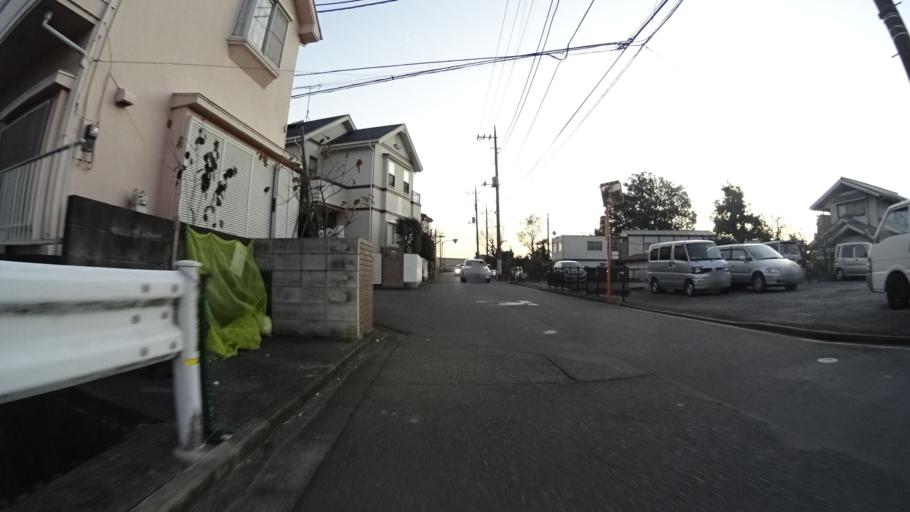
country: JP
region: Tokyo
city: Hino
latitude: 35.6804
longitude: 139.4240
